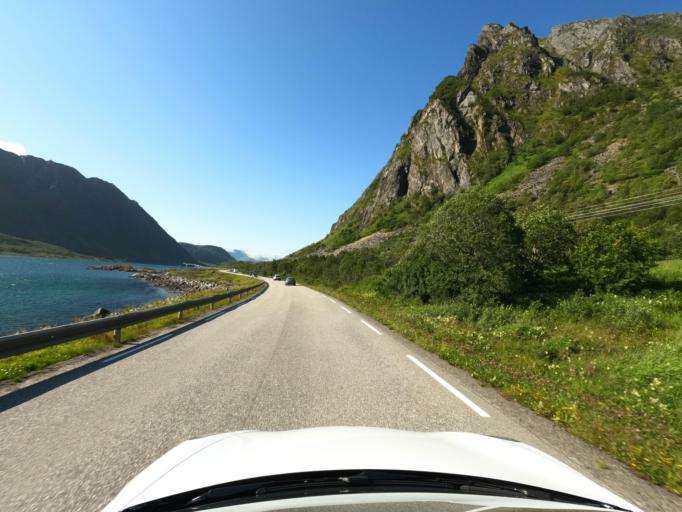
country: NO
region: Nordland
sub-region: Vagan
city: Kabelvag
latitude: 68.2614
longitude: 14.1917
